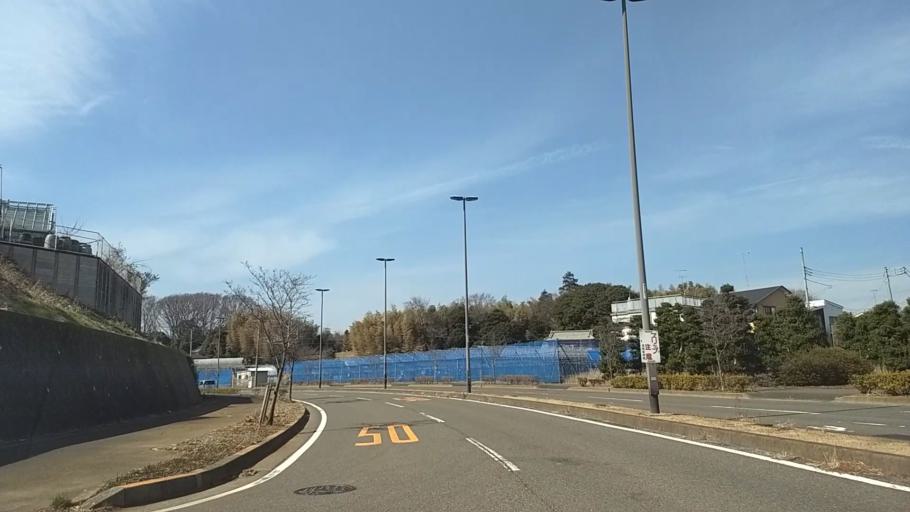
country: JP
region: Kanagawa
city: Fujisawa
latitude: 35.3931
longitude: 139.4242
